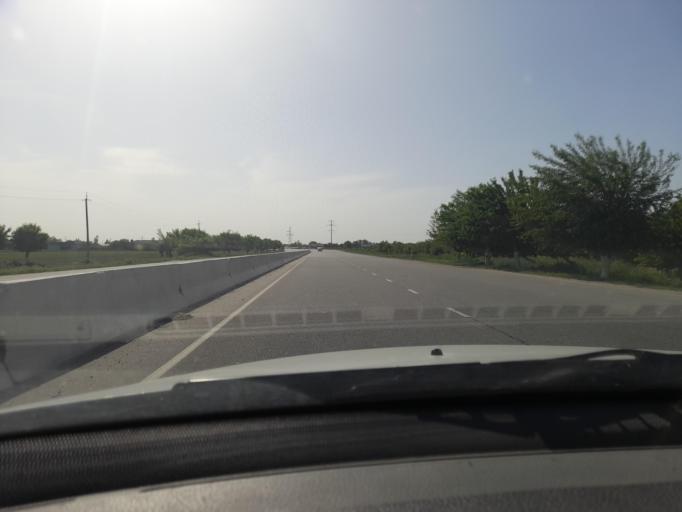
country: UZ
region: Samarqand
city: Ishtixon
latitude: 39.9581
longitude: 66.4661
